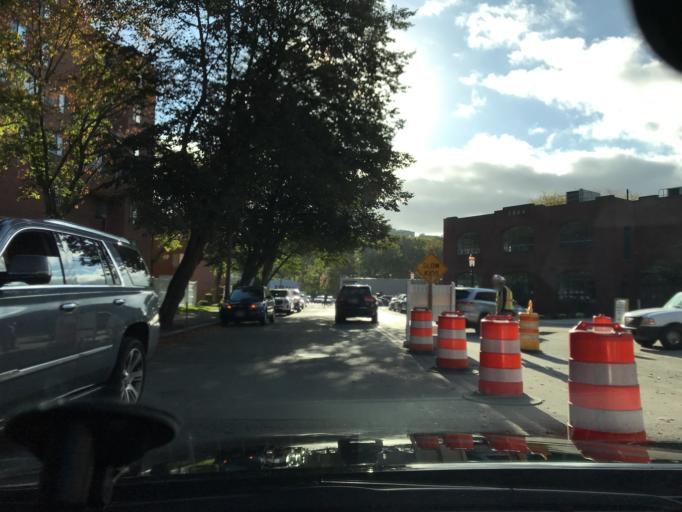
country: US
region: Massachusetts
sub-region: Norfolk County
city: Brookline
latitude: 42.3331
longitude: -71.1148
